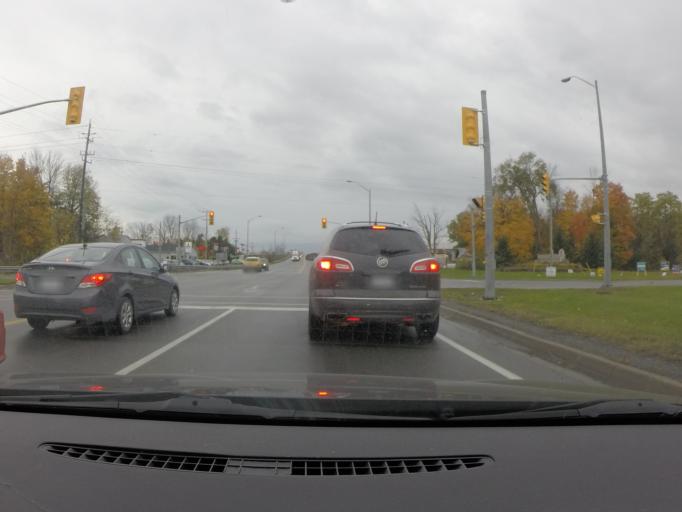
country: CA
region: Ontario
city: Carleton Place
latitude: 45.1281
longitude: -76.1265
